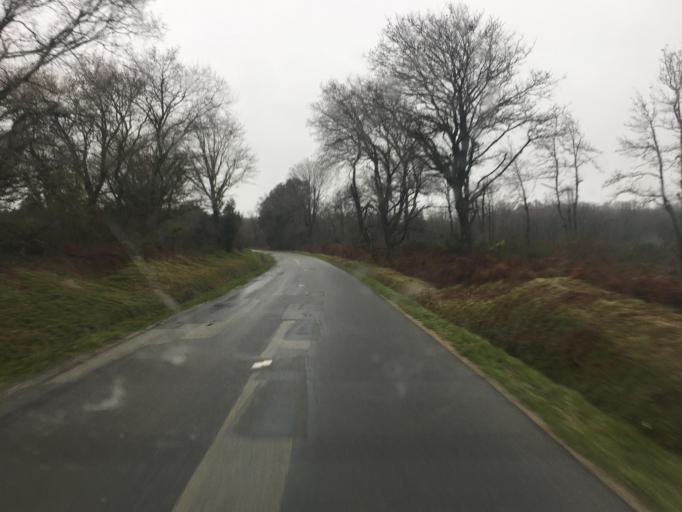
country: FR
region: Brittany
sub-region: Departement du Morbihan
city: Sarzeau
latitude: 47.5241
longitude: -2.6962
